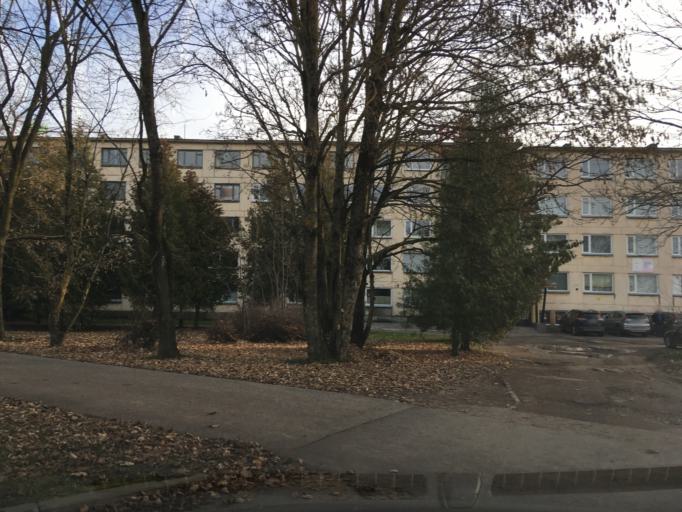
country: EE
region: Ida-Virumaa
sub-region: Johvi vald
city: Johvi
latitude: 59.3513
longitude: 27.4131
